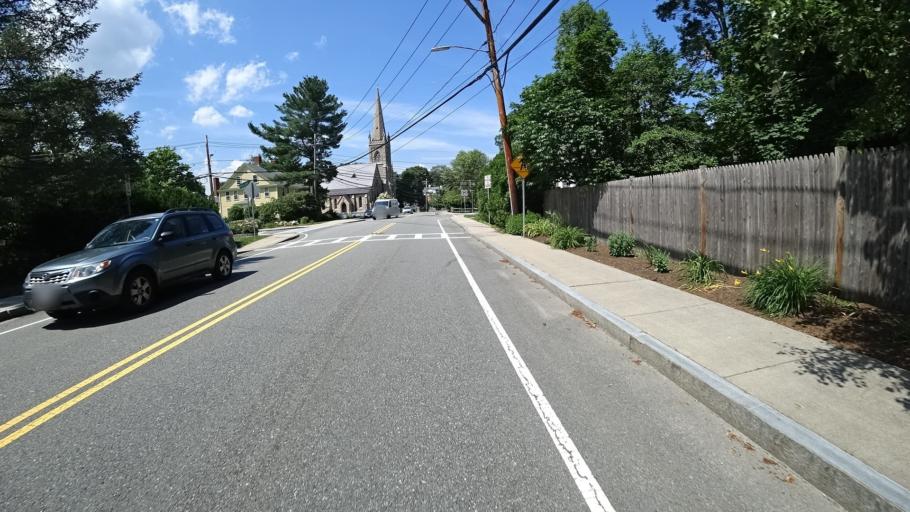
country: US
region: Massachusetts
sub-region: Norfolk County
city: Dedham
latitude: 42.2460
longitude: -71.1775
